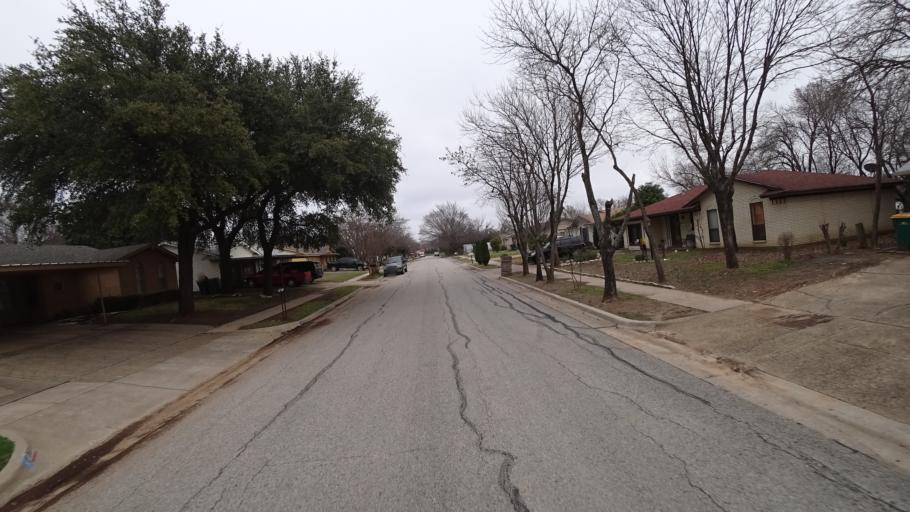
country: US
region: Texas
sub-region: Denton County
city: Lewisville
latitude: 33.0613
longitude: -97.0061
